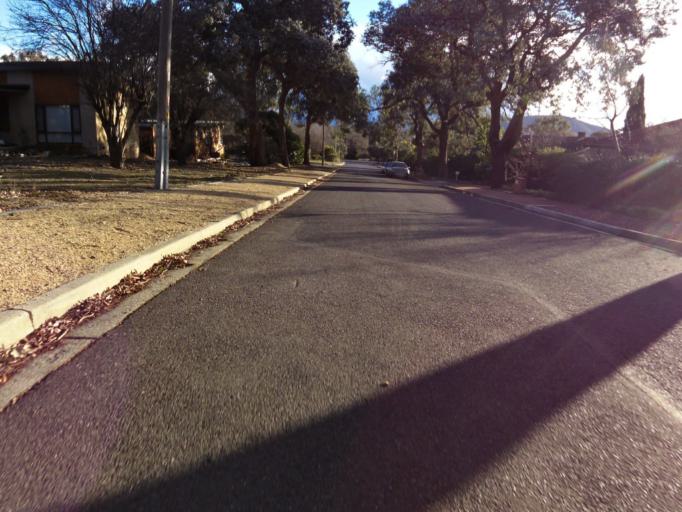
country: AU
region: Australian Capital Territory
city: Canberra
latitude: -35.2721
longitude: 149.1472
